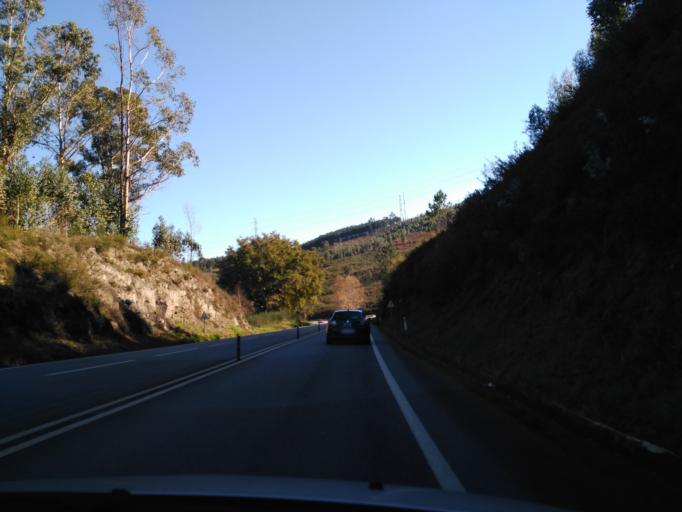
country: PT
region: Braga
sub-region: Povoa de Lanhoso
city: Povoa de Lanhoso
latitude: 41.5847
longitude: -8.3087
